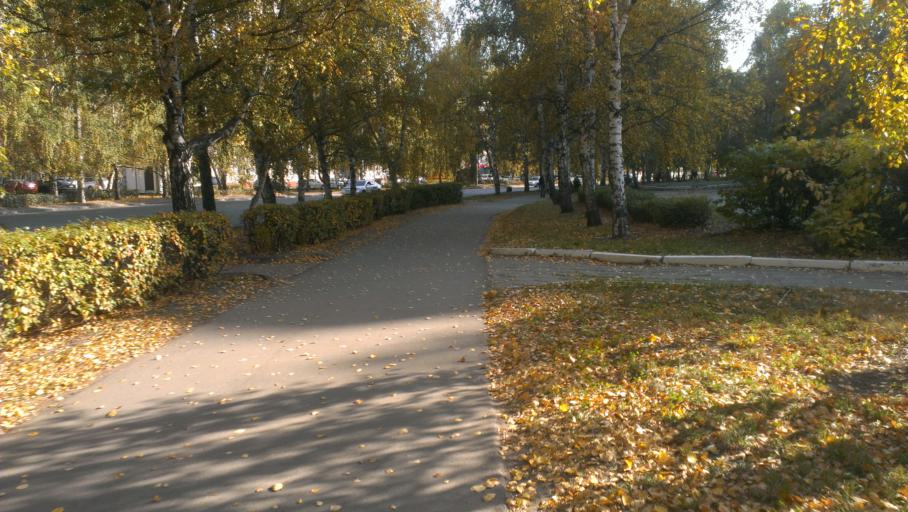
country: RU
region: Altai Krai
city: Novosilikatnyy
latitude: 53.3466
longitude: 83.6841
